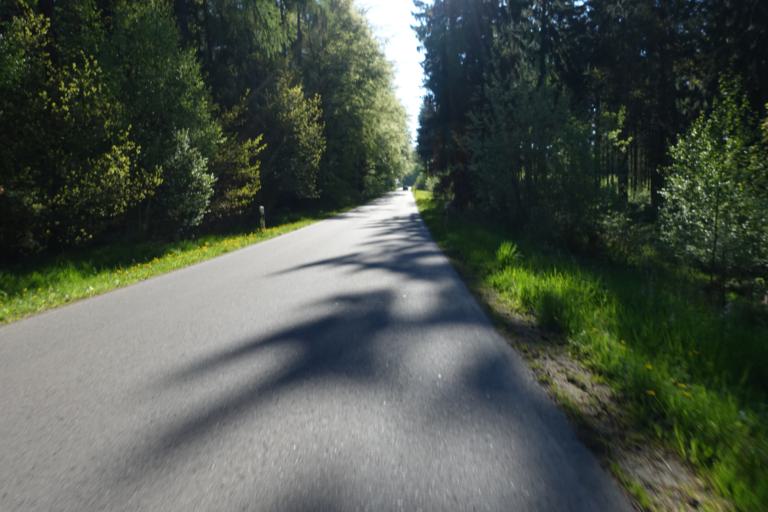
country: DE
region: Saxony
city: Freiberg
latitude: 50.8947
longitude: 13.3798
